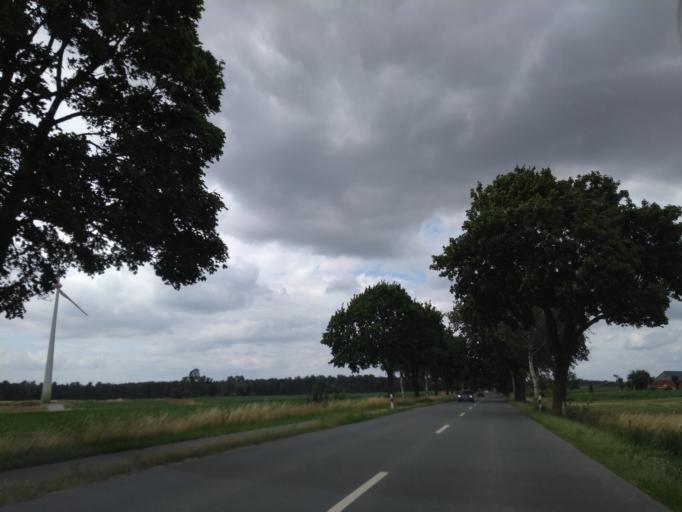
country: DE
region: North Rhine-Westphalia
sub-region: Regierungsbezirk Detmold
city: Salzkotten
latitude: 51.6510
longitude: 8.6682
